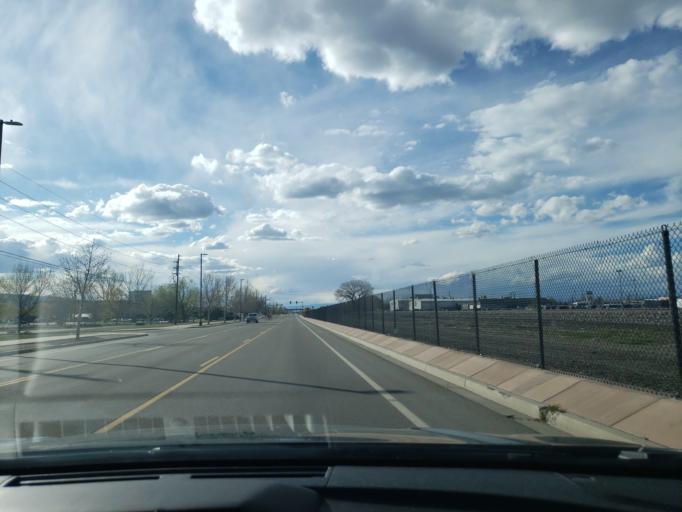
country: US
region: Colorado
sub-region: Mesa County
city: Redlands
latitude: 39.0840
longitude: -108.5955
